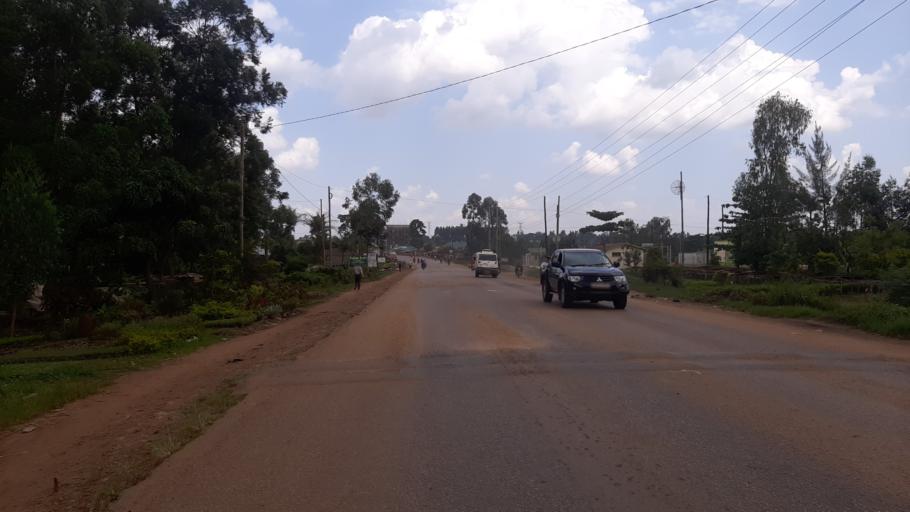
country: UG
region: Eastern Region
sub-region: Mbale District
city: Mbale
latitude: 1.0521
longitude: 34.1784
